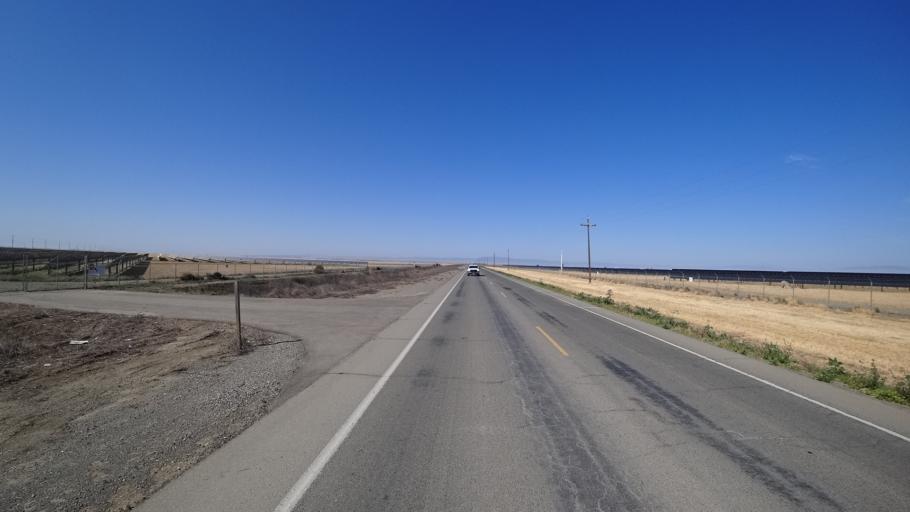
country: US
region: California
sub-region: Kings County
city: Lemoore Station
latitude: 36.2188
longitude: -119.9079
